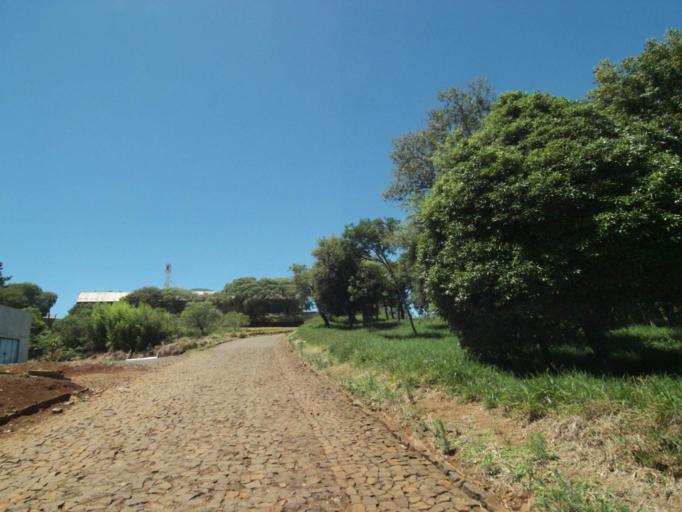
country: BR
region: Parana
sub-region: Pato Branco
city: Pato Branco
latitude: -26.2594
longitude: -52.7728
